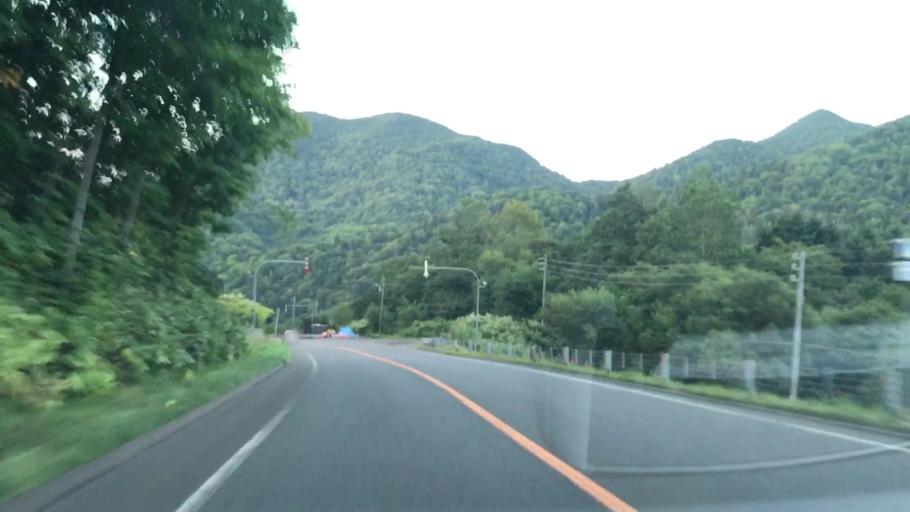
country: JP
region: Hokkaido
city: Sapporo
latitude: 42.9151
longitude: 141.1236
